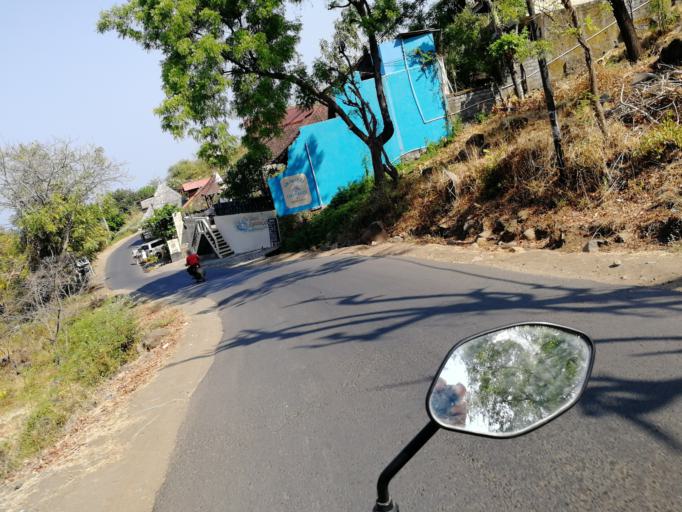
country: ID
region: Bali
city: Biaslantang Kaler
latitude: -8.3400
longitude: 115.6645
